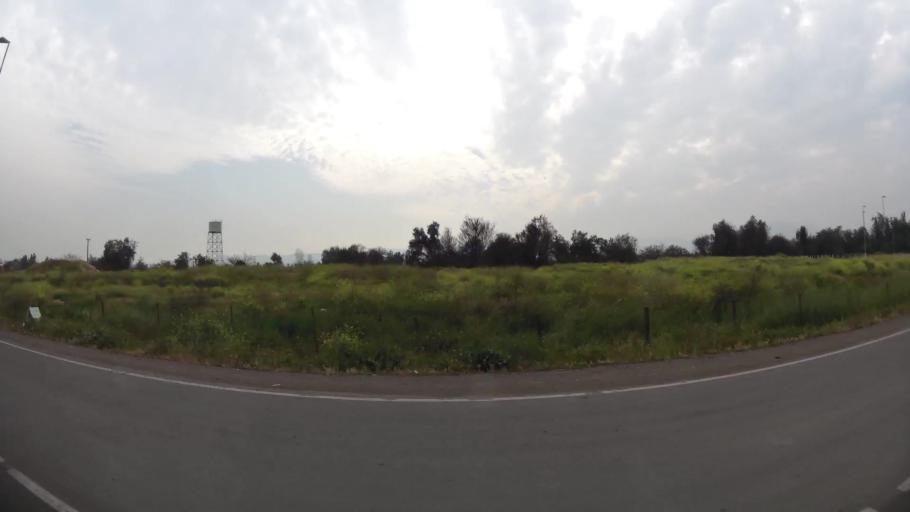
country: CL
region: Santiago Metropolitan
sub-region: Provincia de Chacabuco
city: Chicureo Abajo
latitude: -33.2190
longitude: -70.6770
